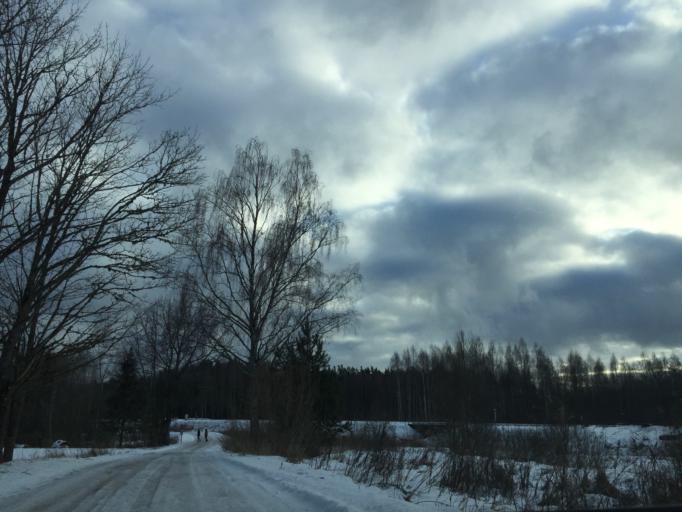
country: LV
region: Lielvarde
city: Lielvarde
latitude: 56.5755
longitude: 24.7972
